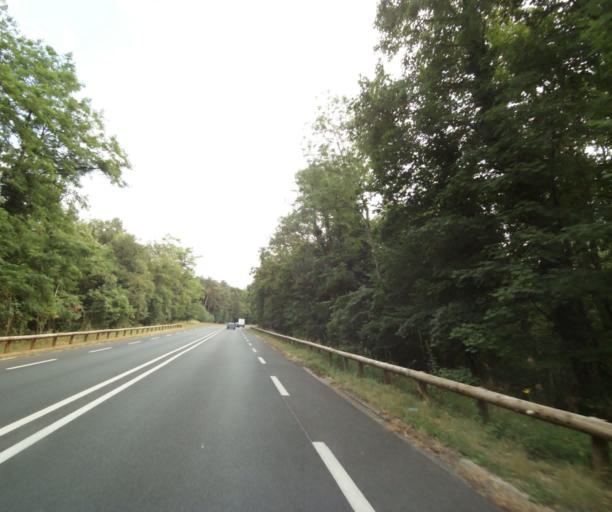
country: FR
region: Ile-de-France
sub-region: Departement de Seine-et-Marne
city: Fontainebleau
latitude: 48.4322
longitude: 2.6996
